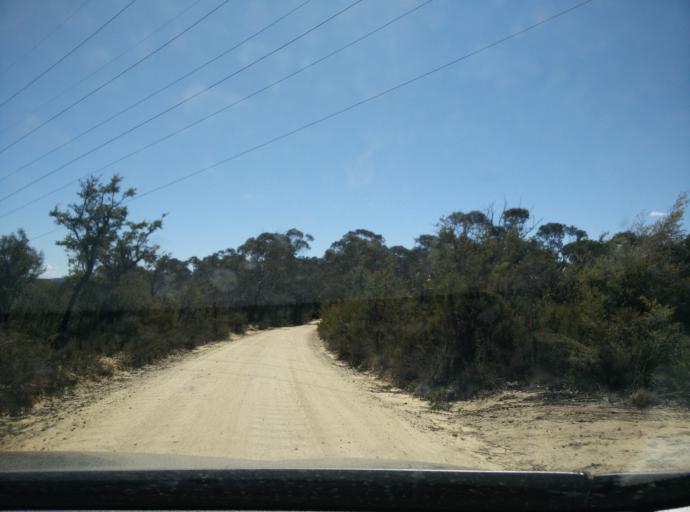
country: AU
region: New South Wales
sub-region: Blue Mountains Municipality
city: Blackheath
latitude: -33.5900
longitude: 150.2684
